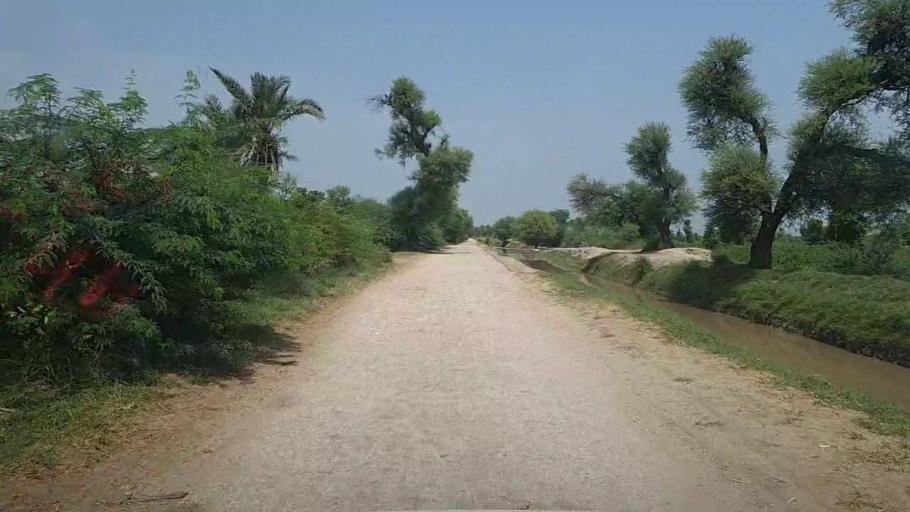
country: PK
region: Sindh
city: Karaundi
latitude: 26.8972
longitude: 68.3318
